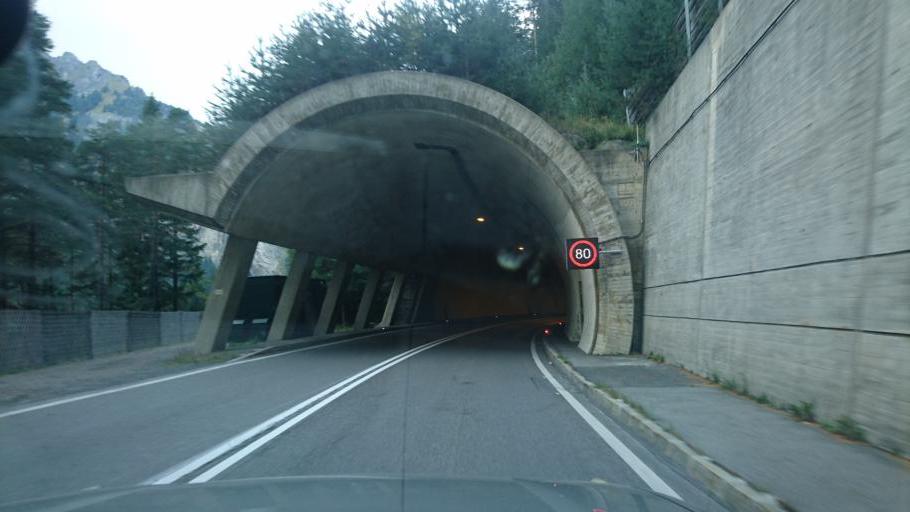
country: AT
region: Tyrol
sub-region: Politischer Bezirk Landeck
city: Nauders
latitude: 46.9179
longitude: 10.4895
